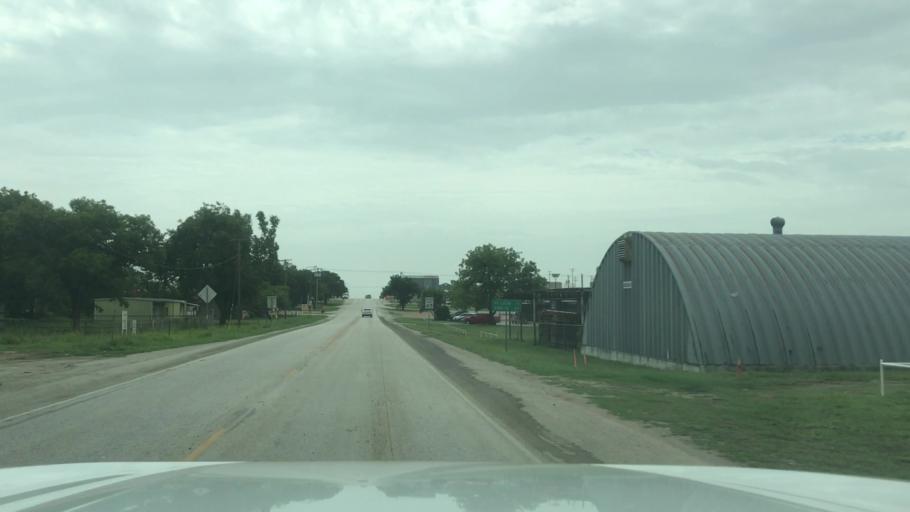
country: US
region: Texas
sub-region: Eastland County
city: Gorman
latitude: 32.2128
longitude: -98.6696
